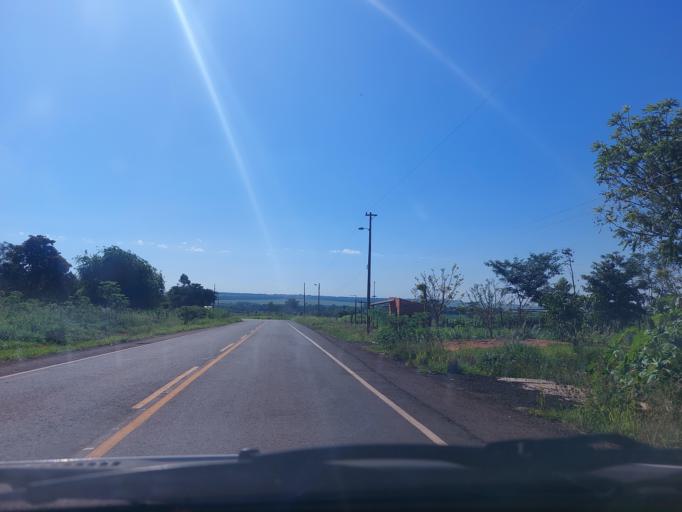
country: PY
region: San Pedro
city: Guayaybi
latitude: -24.3124
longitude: -56.1554
